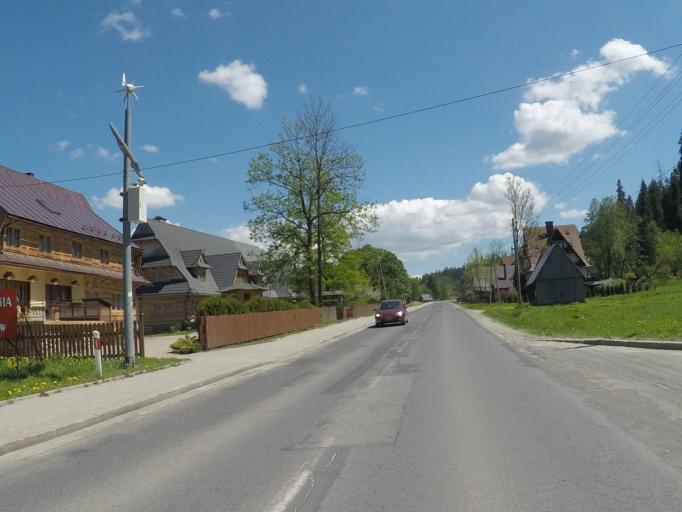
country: PL
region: Lesser Poland Voivodeship
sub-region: Powiat tatrzanski
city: Bukowina Tatrzanska
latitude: 49.3363
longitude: 20.0641
